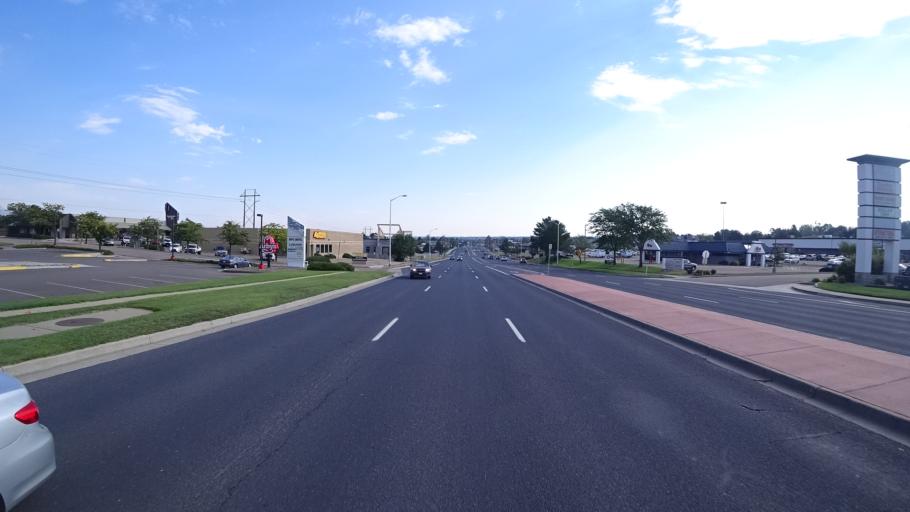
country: US
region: Colorado
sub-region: El Paso County
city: Colorado Springs
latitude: 38.9131
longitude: -104.7879
